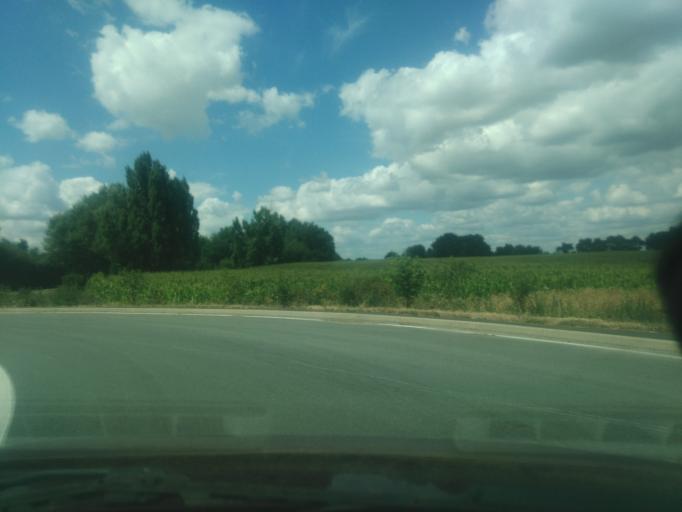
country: FR
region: Pays de la Loire
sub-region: Departement de la Vendee
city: Chauche
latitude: 46.8377
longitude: -1.2833
